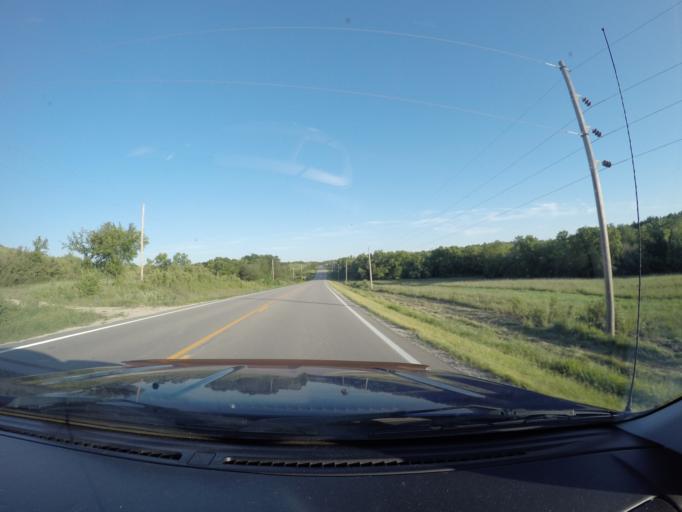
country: US
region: Kansas
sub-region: Pottawatomie County
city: Wamego
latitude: 39.1249
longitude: -96.2944
